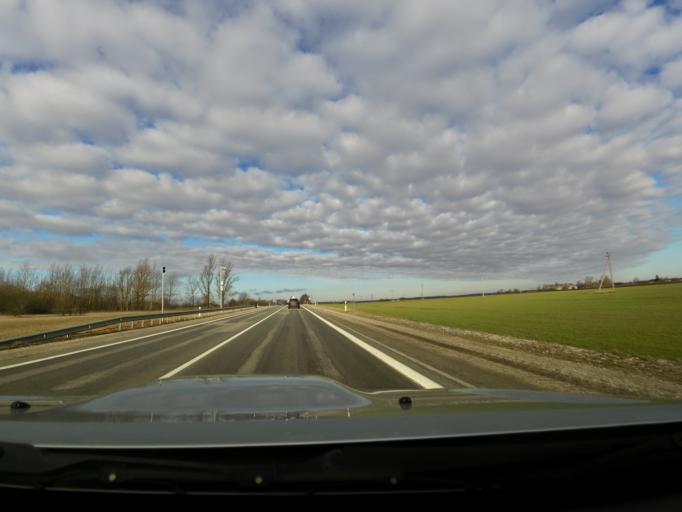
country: LT
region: Panevezys
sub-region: Panevezys City
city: Panevezys
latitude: 55.7497
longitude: 24.1462
